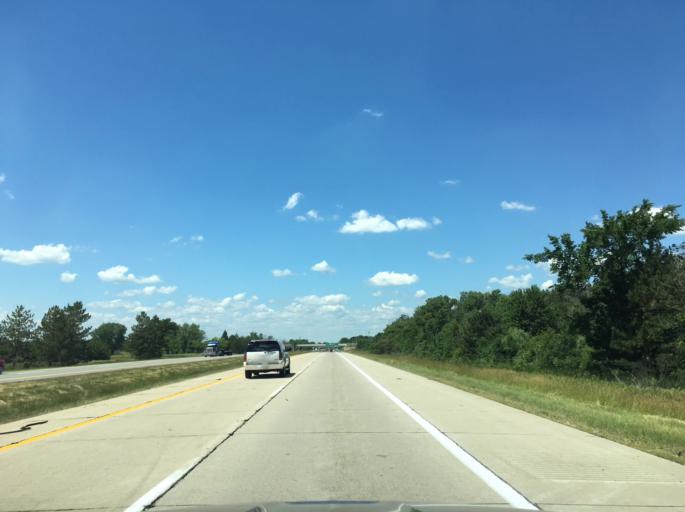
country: US
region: Michigan
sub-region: Bay County
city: Auburn
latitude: 43.5977
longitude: -84.1307
